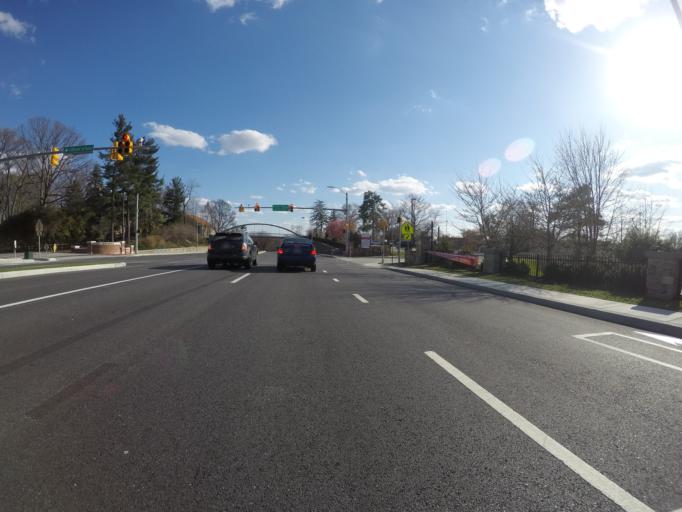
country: US
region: Maryland
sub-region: Baltimore County
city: Towson
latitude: 39.3601
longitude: -76.6352
